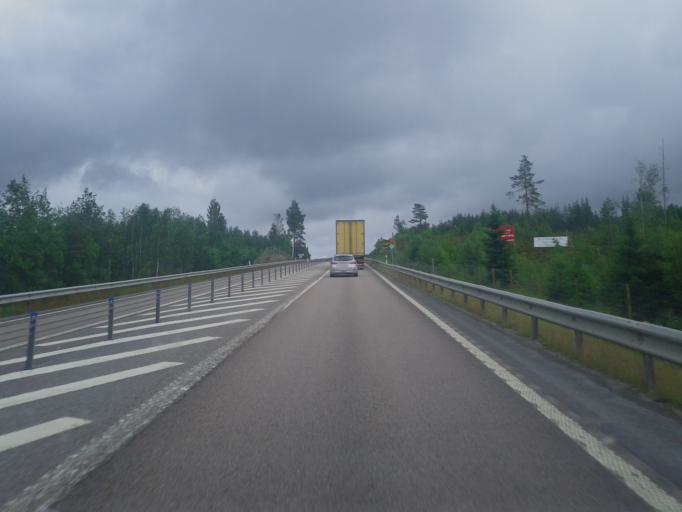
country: SE
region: Vaesternorrland
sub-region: Haernoesands Kommun
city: Haernoesand
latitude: 62.6001
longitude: 17.8113
